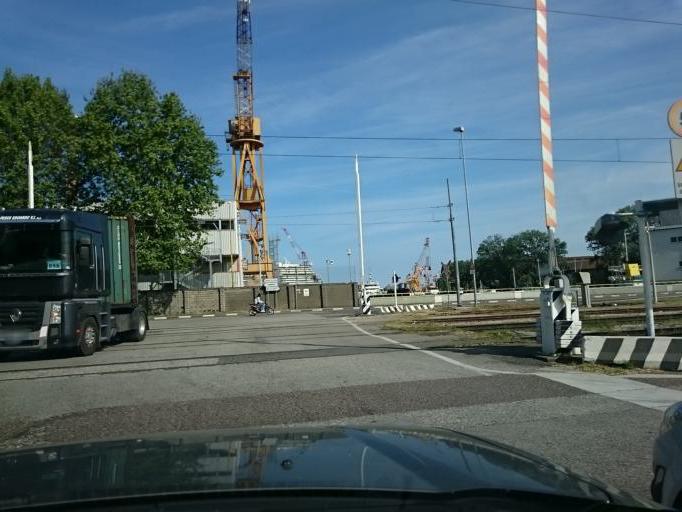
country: IT
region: Veneto
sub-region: Provincia di Venezia
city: Mestre
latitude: 45.4744
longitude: 12.2394
